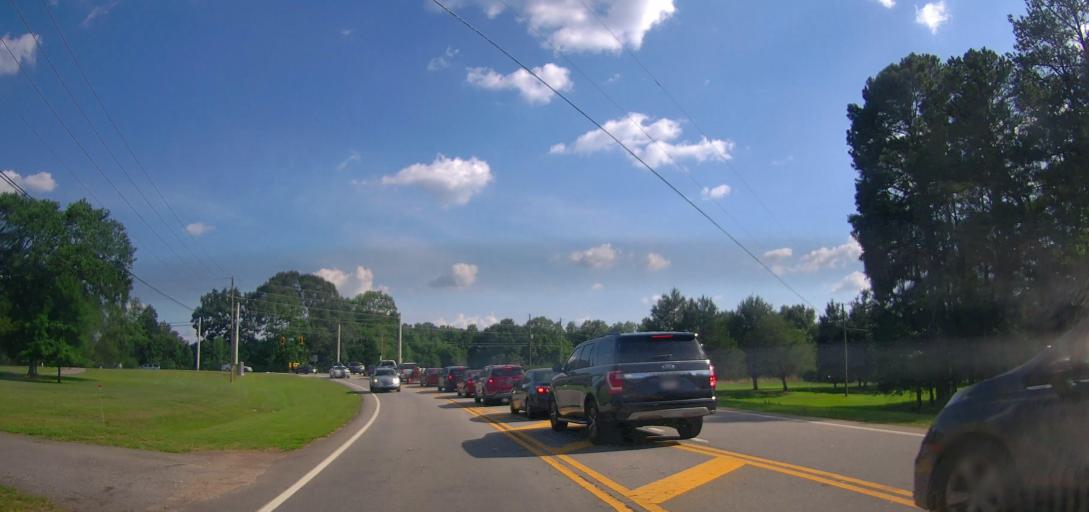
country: US
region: Georgia
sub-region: Henry County
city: McDonough
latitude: 33.4332
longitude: -84.2072
